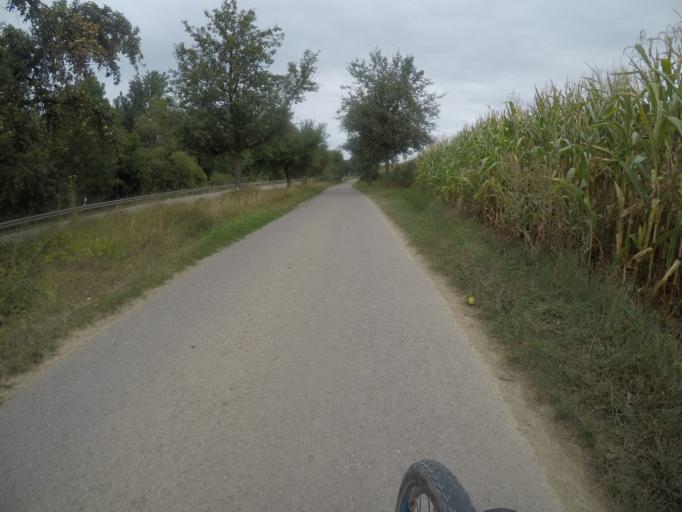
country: DE
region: Baden-Wuerttemberg
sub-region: Regierungsbezirk Stuttgart
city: Oberriexingen
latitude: 48.9315
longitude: 9.0401
